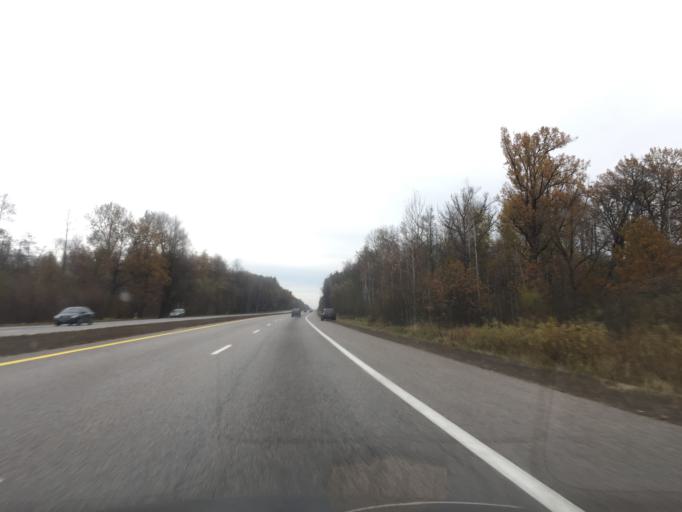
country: BY
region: Gomel
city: Gomel
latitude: 52.3702
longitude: 30.7561
